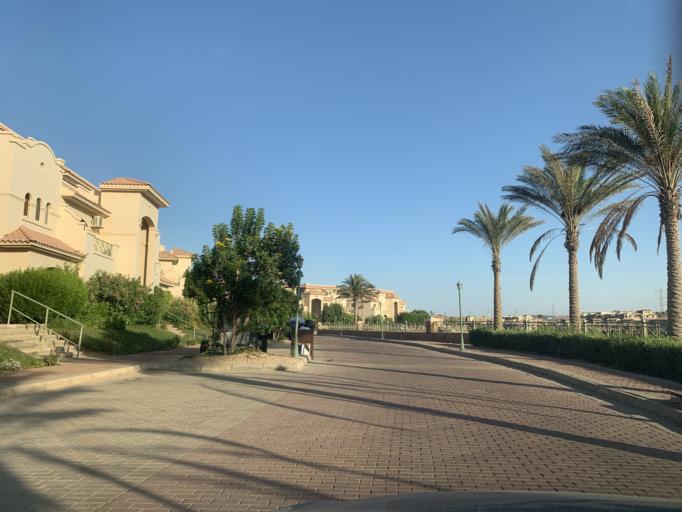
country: EG
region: As Suways
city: Ain Sukhna
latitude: 29.3723
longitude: 32.5686
